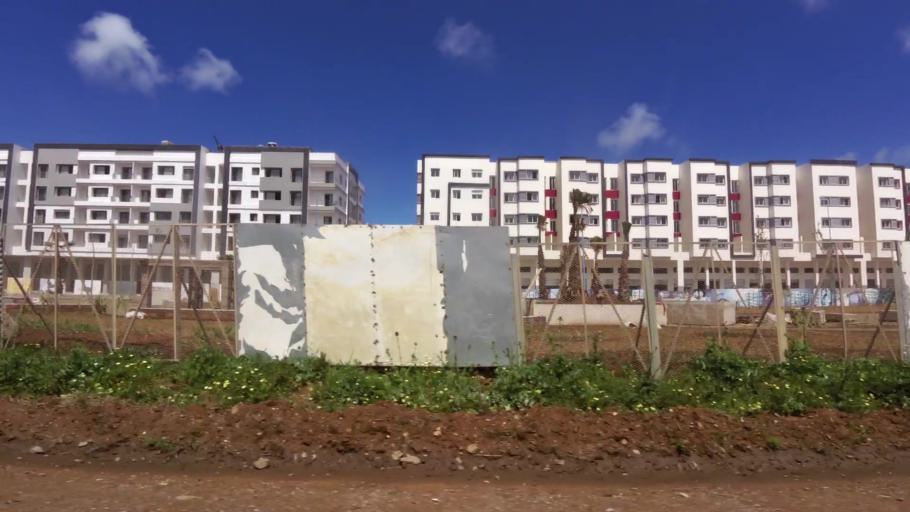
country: MA
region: Grand Casablanca
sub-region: Nouaceur
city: Dar Bouazza
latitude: 33.5289
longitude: -7.7333
